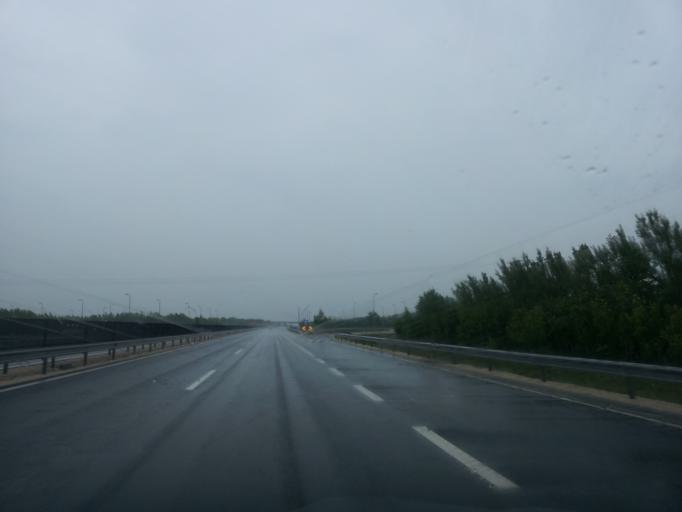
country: HU
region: Tolna
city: Dunaszentgyorgy
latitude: 46.5444
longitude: 18.7879
